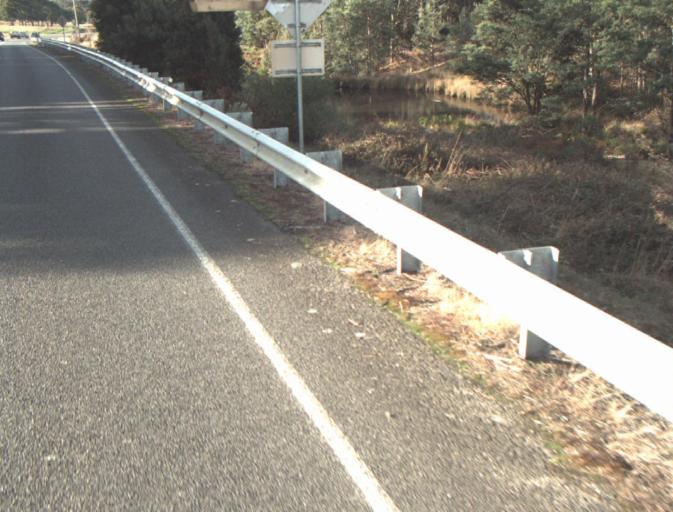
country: AU
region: Tasmania
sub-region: Launceston
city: Mayfield
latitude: -41.2848
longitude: 147.2183
